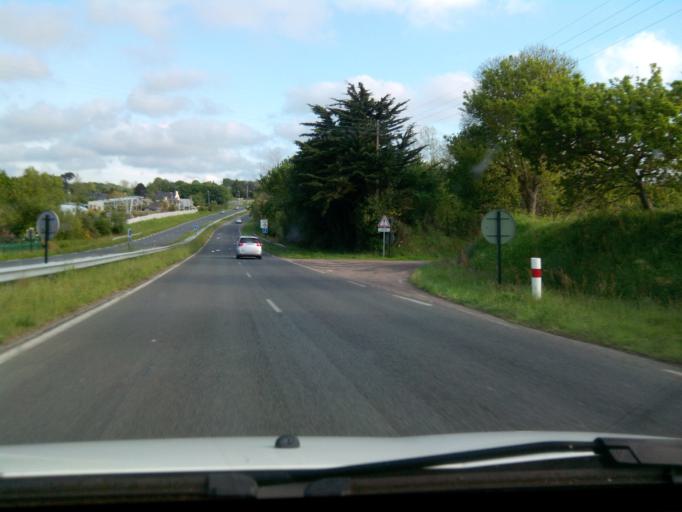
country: FR
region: Brittany
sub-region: Departement des Cotes-d'Armor
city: Saint-Quay-Perros
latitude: 48.7773
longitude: -3.4477
